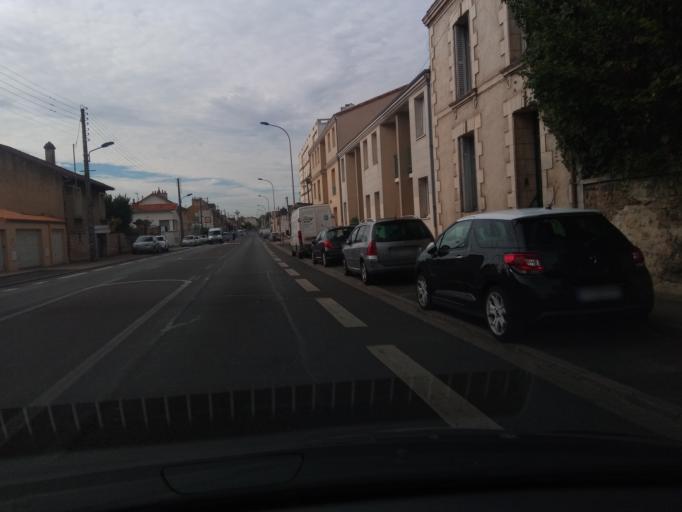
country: FR
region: Poitou-Charentes
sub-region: Departement de la Vienne
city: Biard
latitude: 46.5669
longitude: 0.3195
